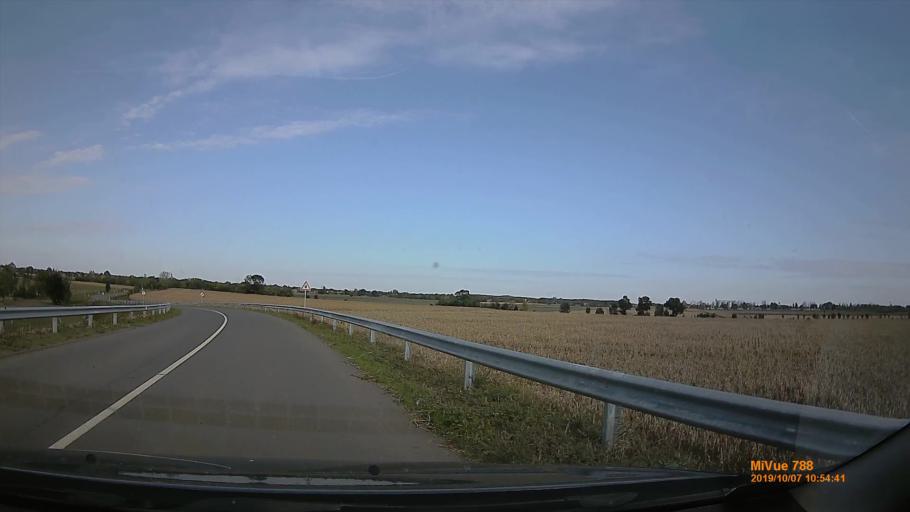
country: HU
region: Bekes
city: Kondoros
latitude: 46.7386
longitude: 20.8081
